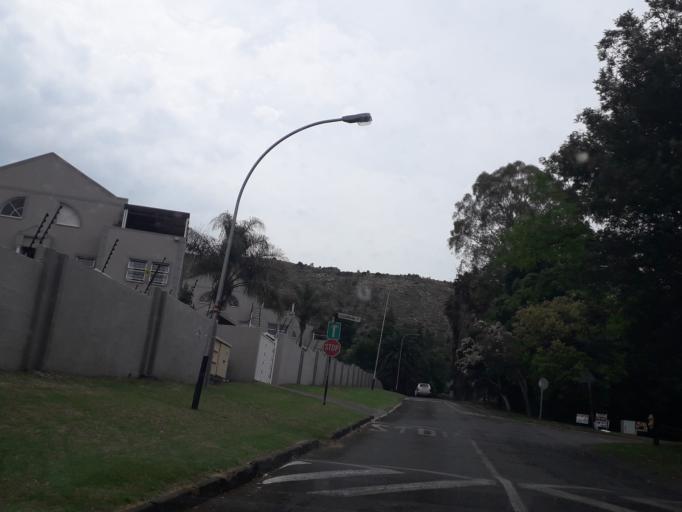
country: ZA
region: Gauteng
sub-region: City of Johannesburg Metropolitan Municipality
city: Johannesburg
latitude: -26.1728
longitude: 28.1146
